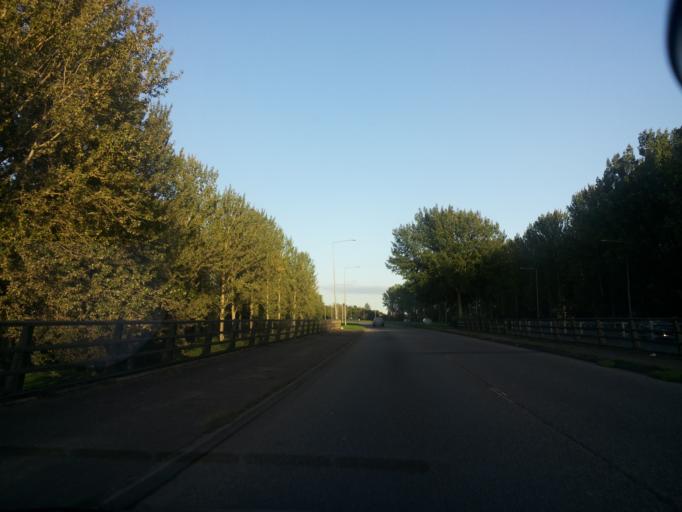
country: GB
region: England
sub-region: Milton Keynes
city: Broughton
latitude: 52.0469
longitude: -0.7201
